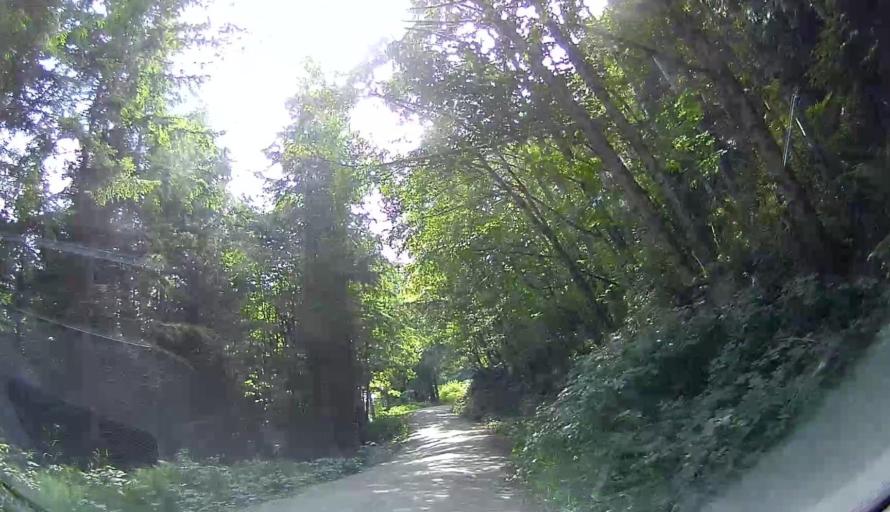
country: US
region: Washington
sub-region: Whatcom County
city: Sudden Valley
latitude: 48.6137
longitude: -122.3900
